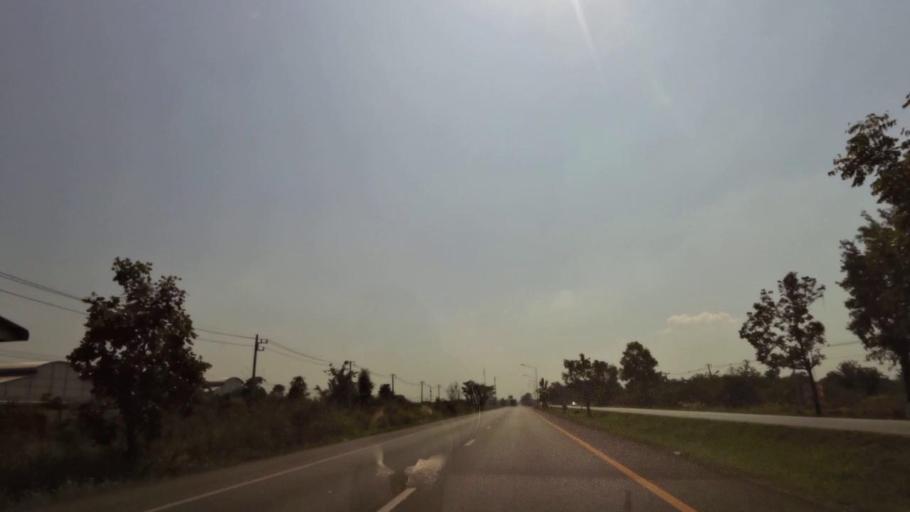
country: TH
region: Phichit
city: Bueng Na Rang
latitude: 16.2771
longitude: 100.1271
